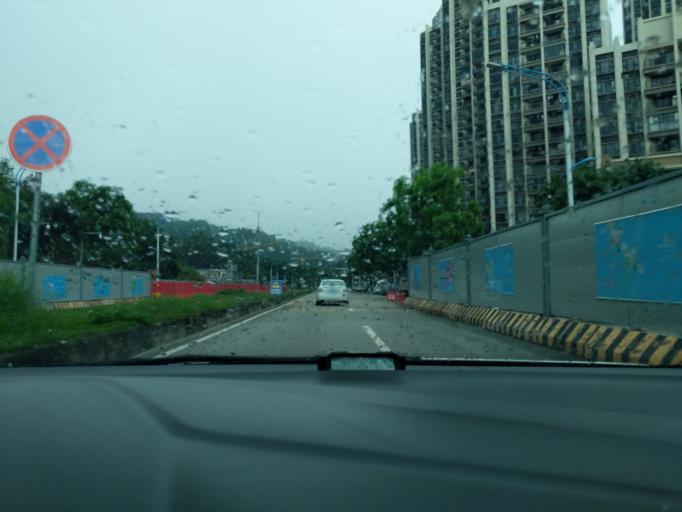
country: CN
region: Guangdong
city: Huangge
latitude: 22.7976
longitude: 113.5150
